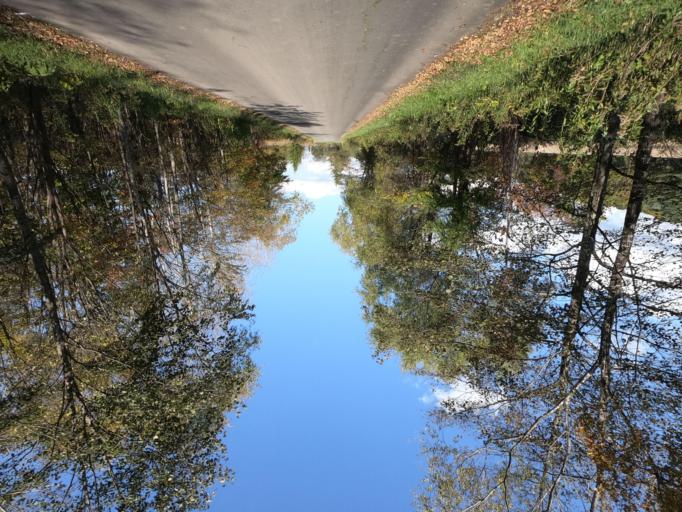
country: JP
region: Hokkaido
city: Otofuke
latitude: 43.2333
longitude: 143.2644
